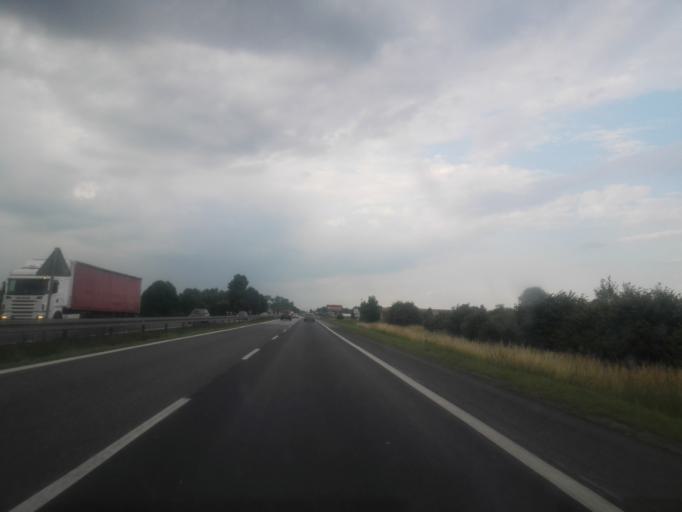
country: PL
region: Silesian Voivodeship
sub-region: Powiat czestochowski
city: Kamienica Polska
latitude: 50.6810
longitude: 19.1287
